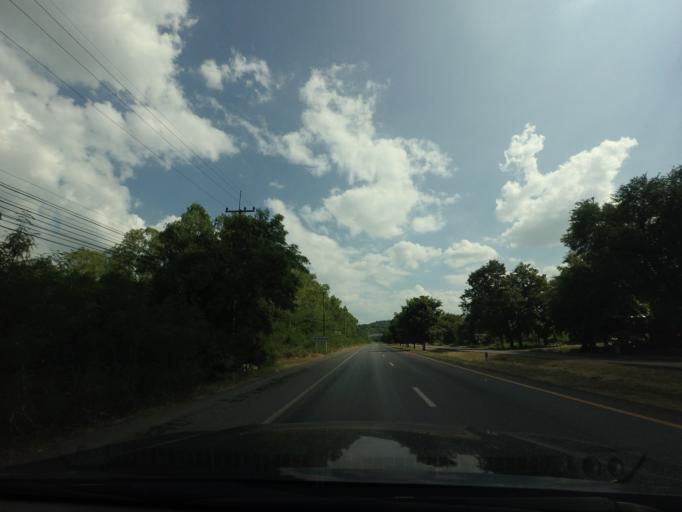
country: TH
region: Phetchabun
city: Wichian Buri
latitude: 15.6355
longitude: 101.0464
